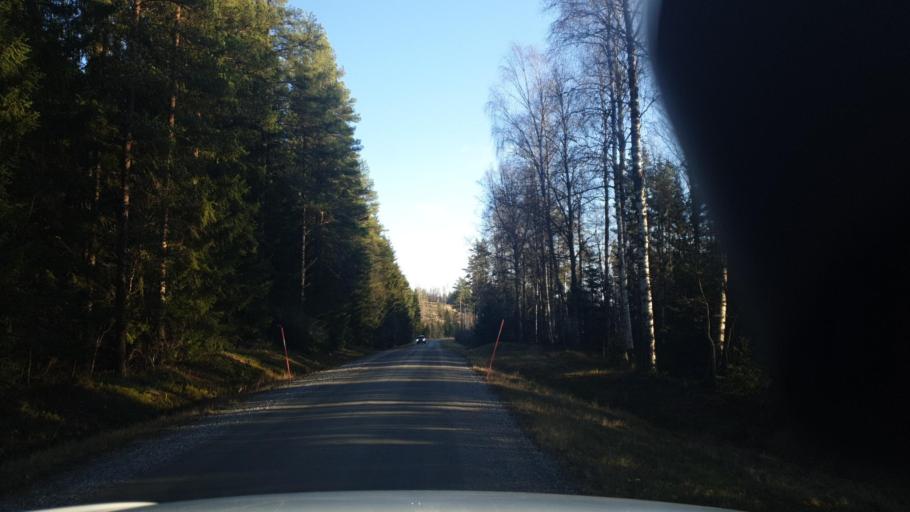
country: SE
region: Vaermland
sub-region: Arvika Kommun
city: Arvika
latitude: 59.8752
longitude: 12.6963
